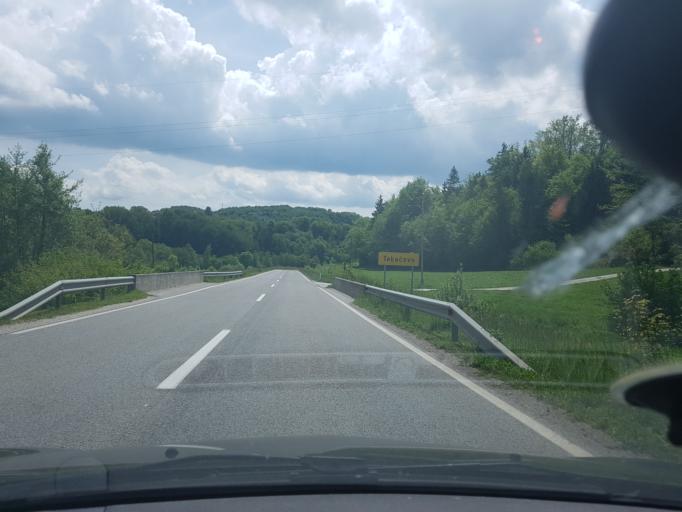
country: SI
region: Rogaska Slatina
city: Rogaska Slatina
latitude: 46.2460
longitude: 15.6050
